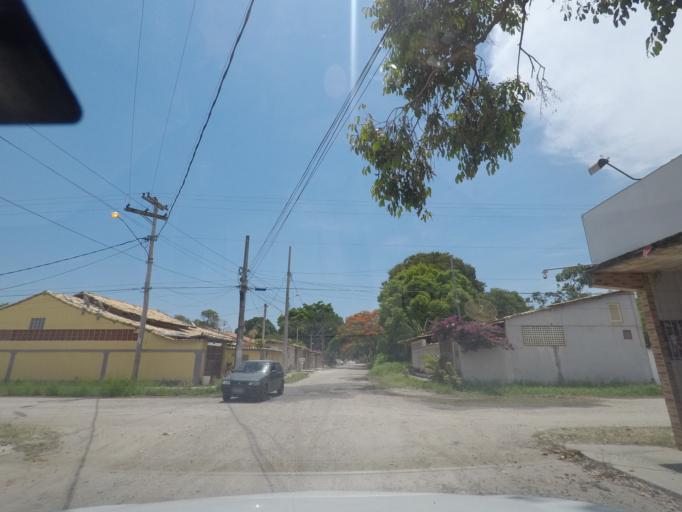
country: BR
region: Rio de Janeiro
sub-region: Marica
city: Marica
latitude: -22.9544
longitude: -42.9611
